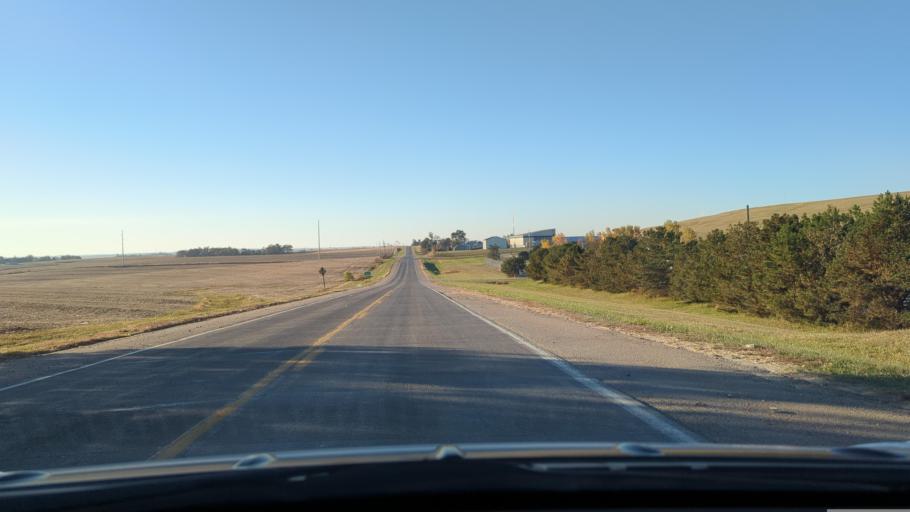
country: US
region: Nebraska
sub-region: Sarpy County
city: Springfield
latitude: 41.1029
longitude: -96.1577
